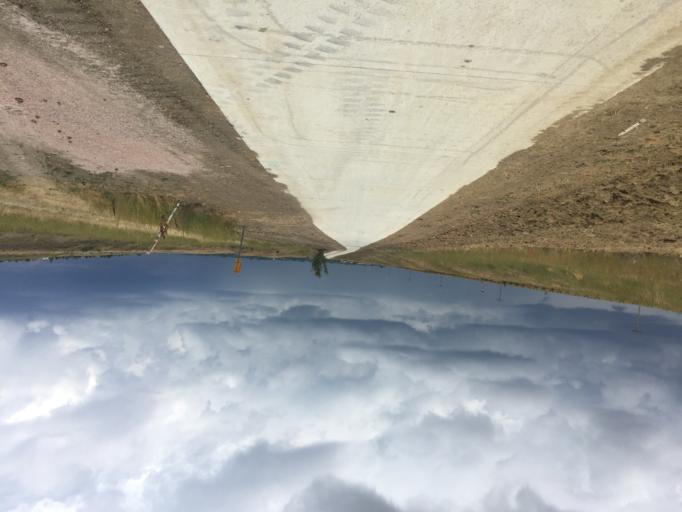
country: US
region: Colorado
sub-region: Larimer County
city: Loveland
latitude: 40.4724
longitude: -105.0958
